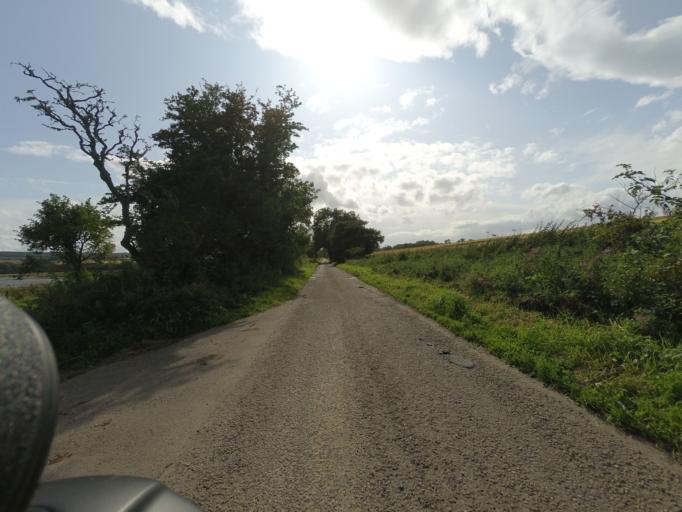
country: GB
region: Scotland
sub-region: Highland
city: Invergordon
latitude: 57.6665
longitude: -4.1668
